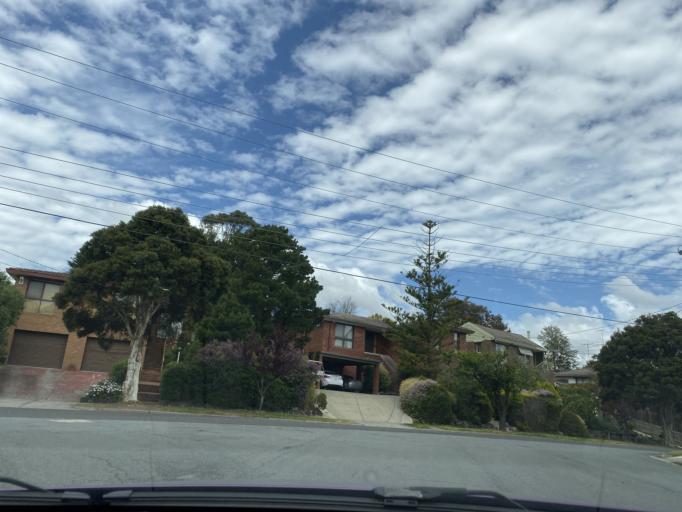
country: AU
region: Victoria
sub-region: Manningham
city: Templestowe Lower
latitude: -37.7674
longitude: 145.1269
